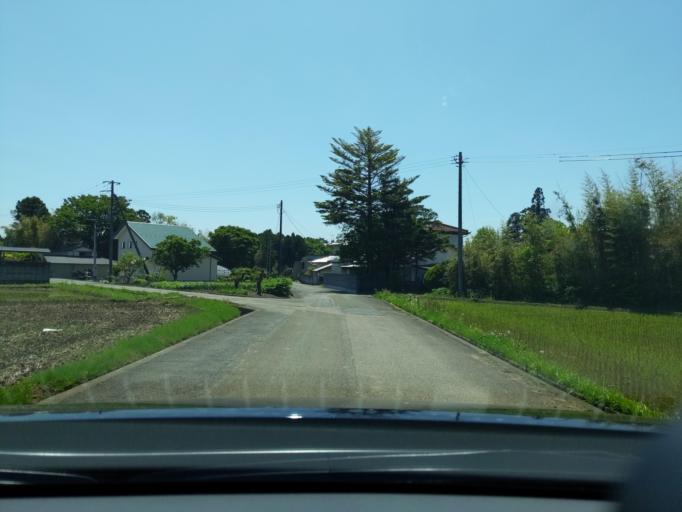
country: JP
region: Fukushima
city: Koriyama
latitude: 37.3904
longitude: 140.2892
